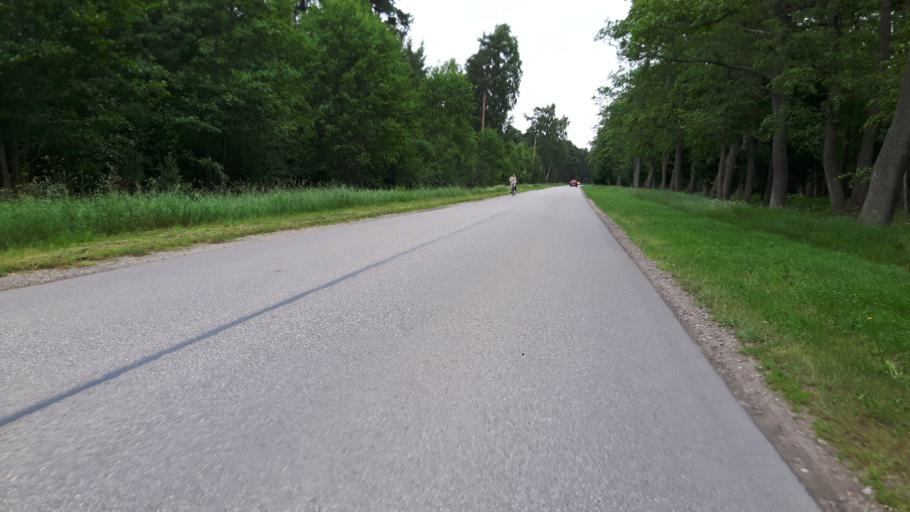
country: LV
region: Liepaja
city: Vec-Liepaja
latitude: 56.5647
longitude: 21.0151
